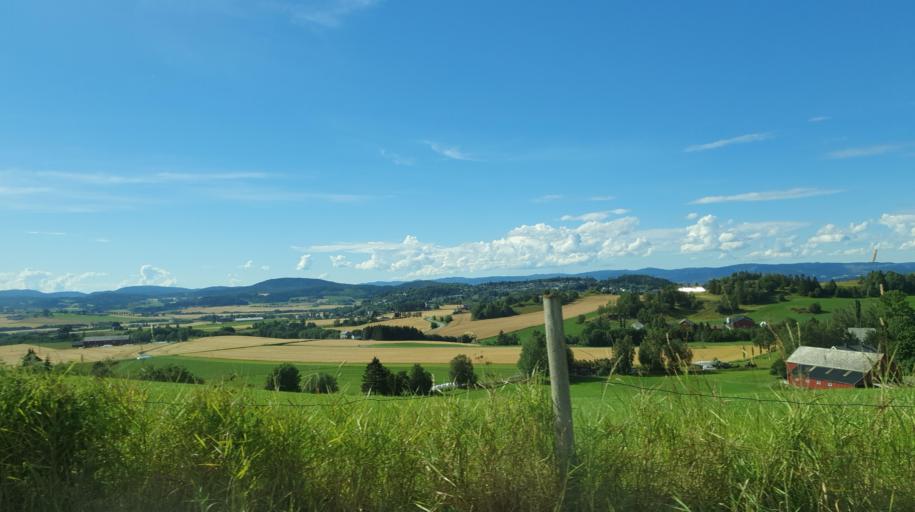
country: NO
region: Nord-Trondelag
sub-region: Levanger
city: Skogn
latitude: 63.6955
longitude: 11.2353
